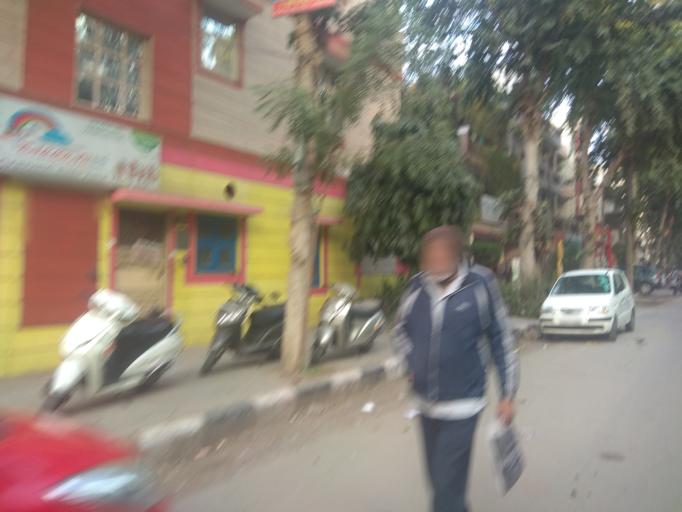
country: IN
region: NCT
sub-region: West Delhi
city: Nangloi Jat
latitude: 28.6318
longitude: 77.0691
